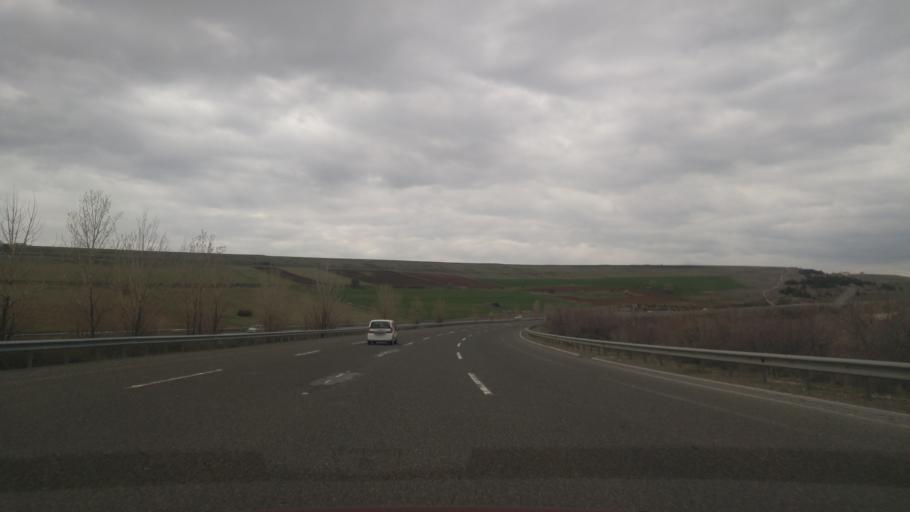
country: TR
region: Ankara
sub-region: Goelbasi
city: Golbasi
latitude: 39.8081
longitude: 32.8690
